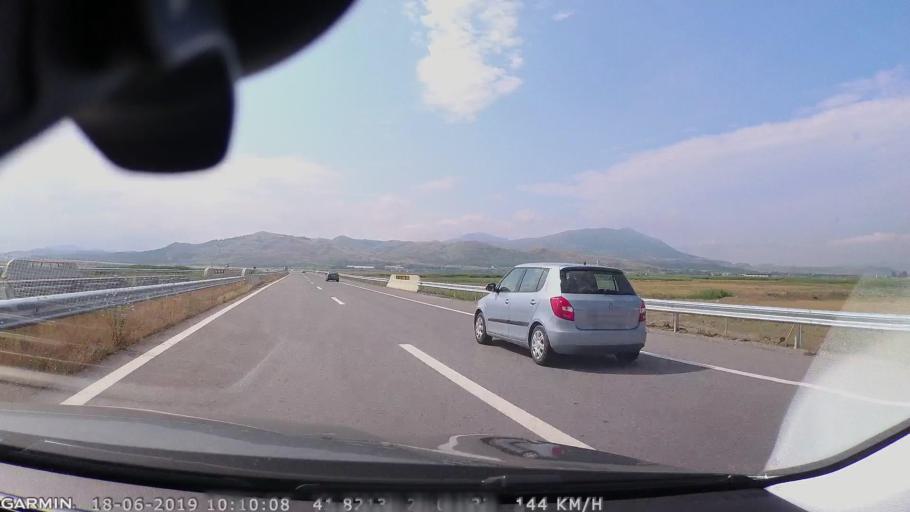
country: MK
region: Sveti Nikole
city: Sveti Nikole
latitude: 41.8368
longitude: 21.9860
